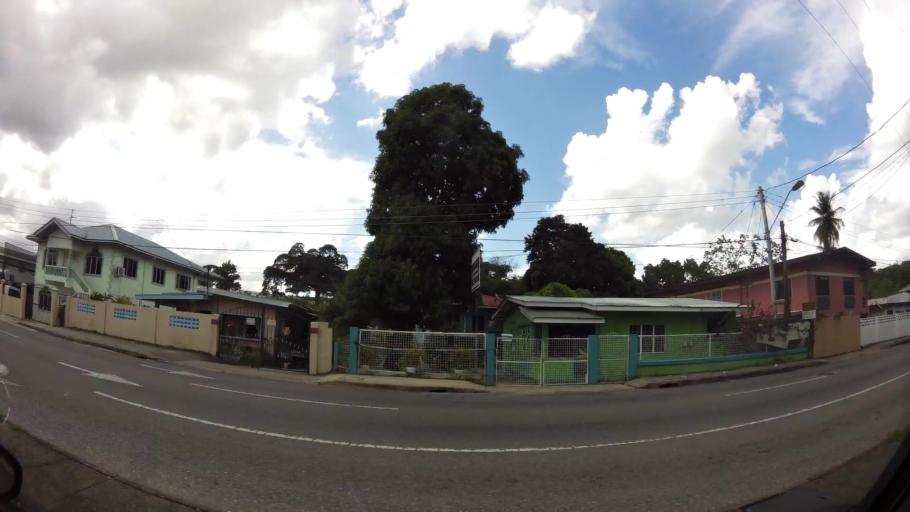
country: TT
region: City of San Fernando
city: San Fernando
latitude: 10.2705
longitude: -61.4685
